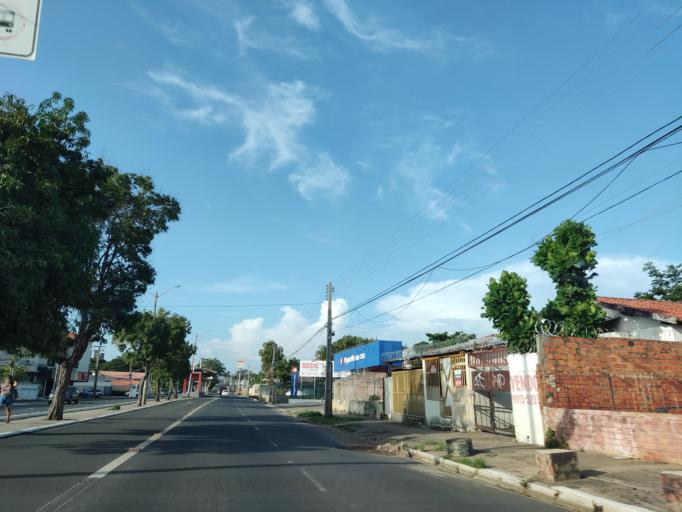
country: BR
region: Piaui
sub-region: Teresina
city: Teresina
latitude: -5.0794
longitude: -42.7744
